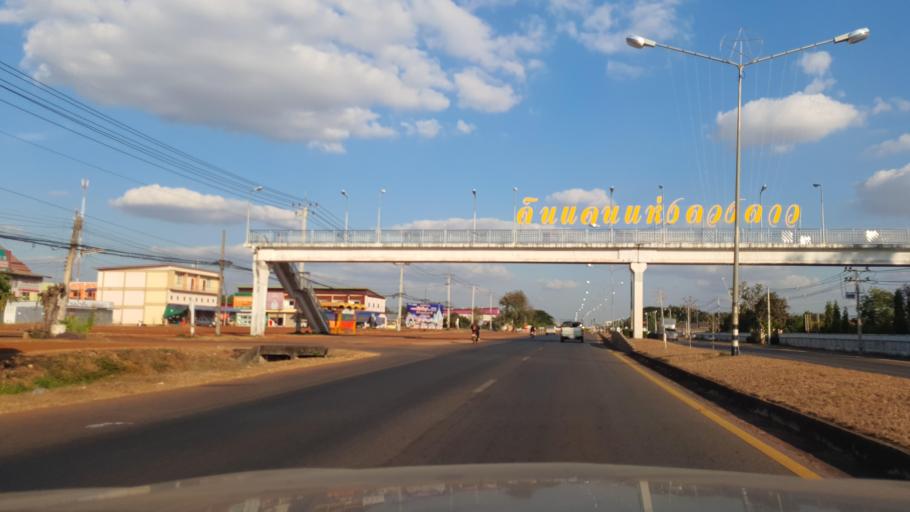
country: TH
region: Sakon Nakhon
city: Sakon Nakhon
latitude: 17.2567
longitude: 104.1718
